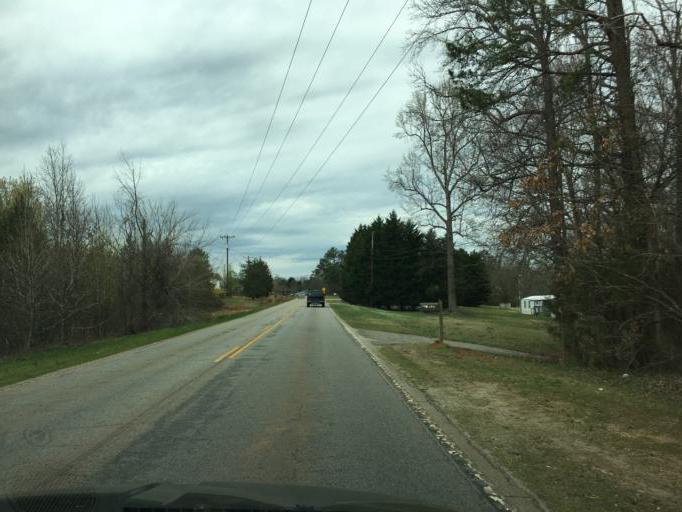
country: US
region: South Carolina
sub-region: Anderson County
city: Piedmont
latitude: 34.7037
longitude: -82.4341
